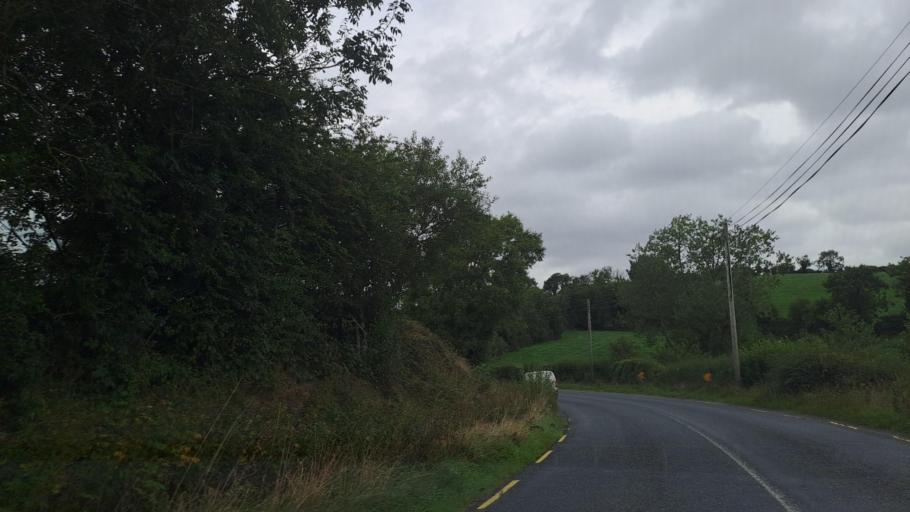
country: IE
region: Ulster
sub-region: An Cabhan
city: Bailieborough
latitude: 53.9721
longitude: -6.9128
